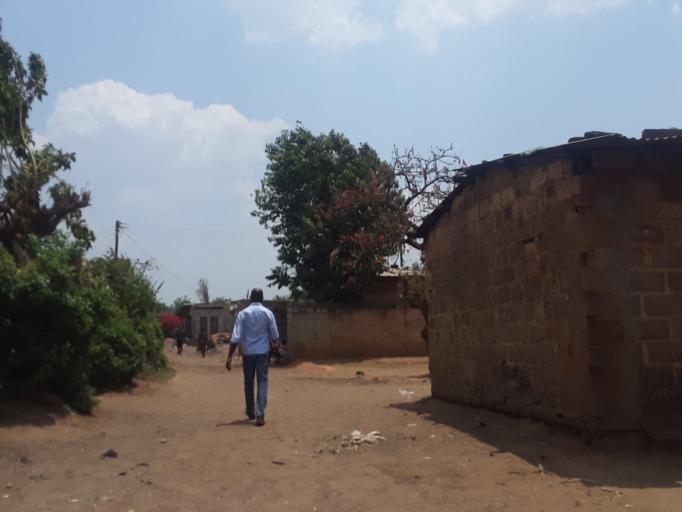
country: ZM
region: Lusaka
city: Lusaka
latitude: -15.3664
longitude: 28.3001
